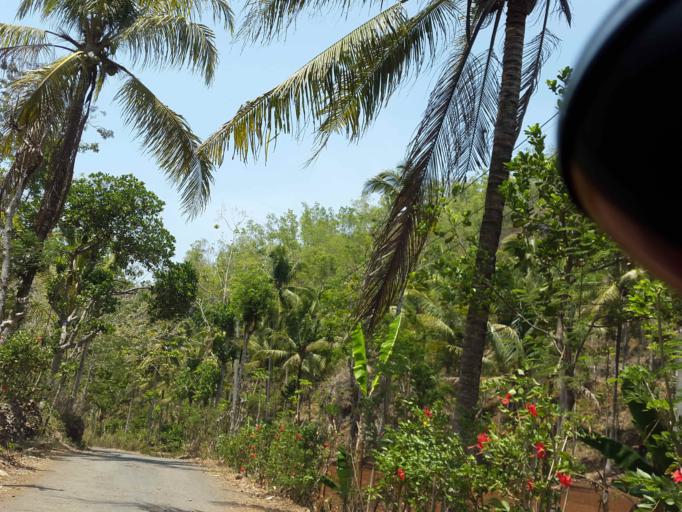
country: ID
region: East Java
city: Krajan
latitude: -8.2016
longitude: 110.9640
